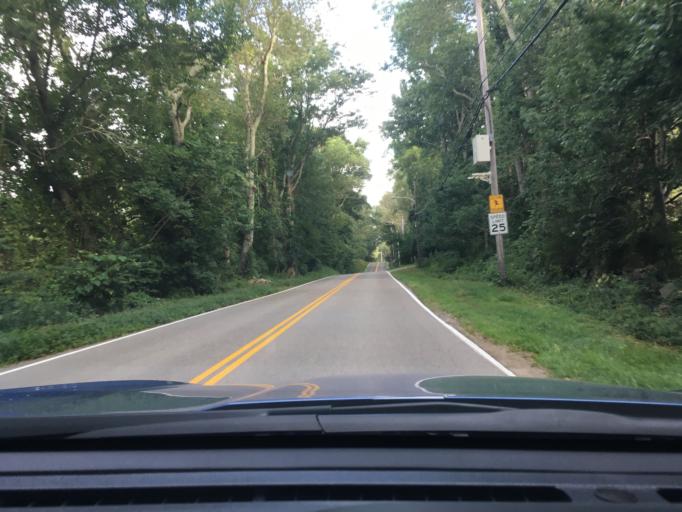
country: US
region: Rhode Island
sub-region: Washington County
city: Exeter
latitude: 41.6248
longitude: -71.5119
